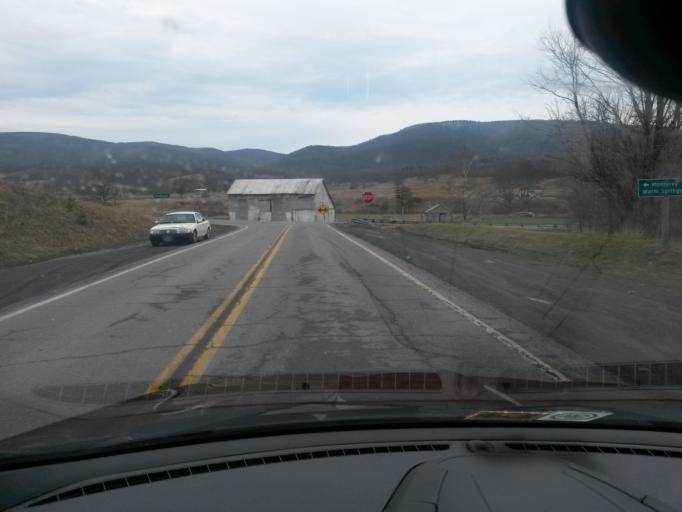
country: US
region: Virginia
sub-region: Highland County
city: Monterey
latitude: 38.3696
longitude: -79.6258
